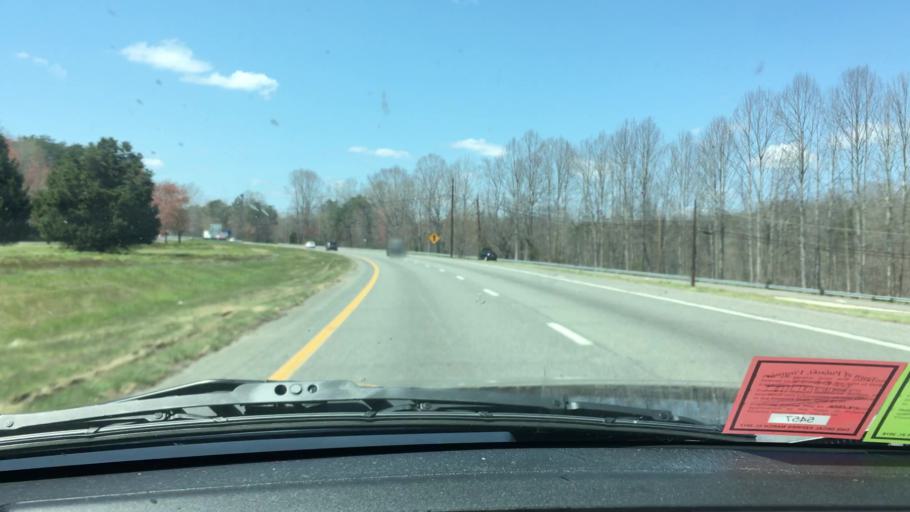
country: US
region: North Carolina
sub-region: Surry County
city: Pilot Mountain
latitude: 36.4005
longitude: -80.4919
